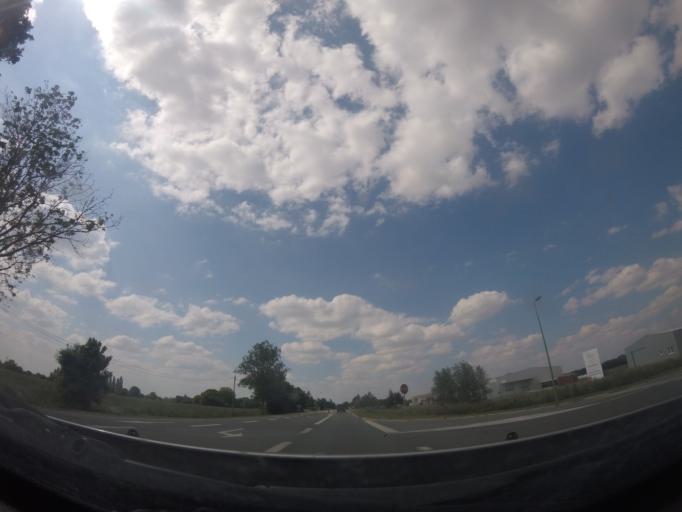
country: FR
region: Poitou-Charentes
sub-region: Departement de la Charente-Maritime
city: Bords
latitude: 45.8538
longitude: -0.8271
